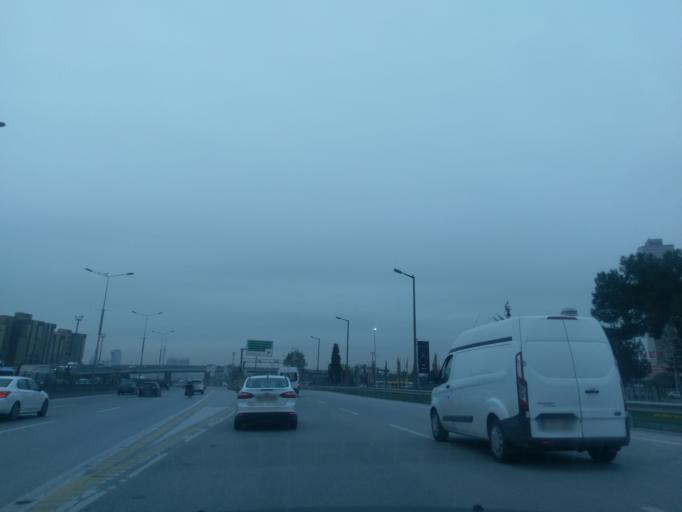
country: TR
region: Istanbul
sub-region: Atasehir
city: Atasehir
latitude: 40.9779
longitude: 29.0977
